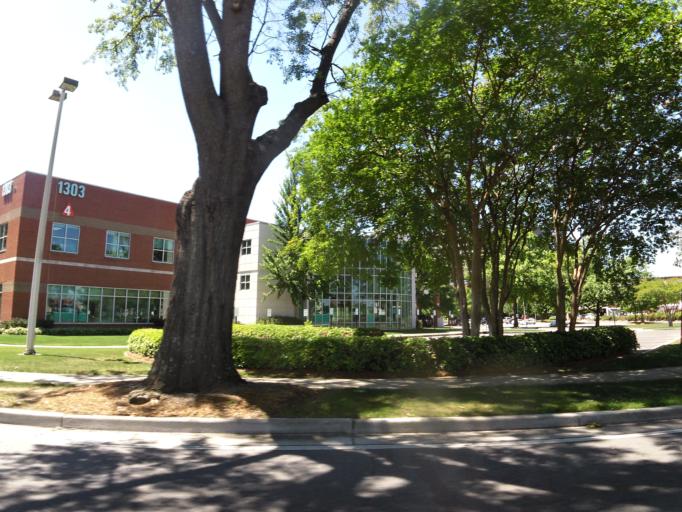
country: US
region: Georgia
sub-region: Richmond County
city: Augusta
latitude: 33.4727
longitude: -81.9806
